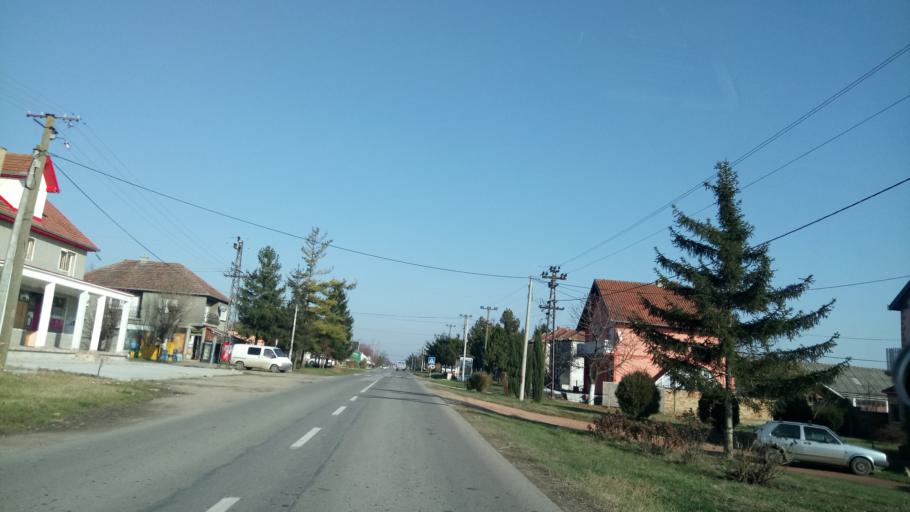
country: RS
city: Ljukovo
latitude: 45.0180
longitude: 20.0303
